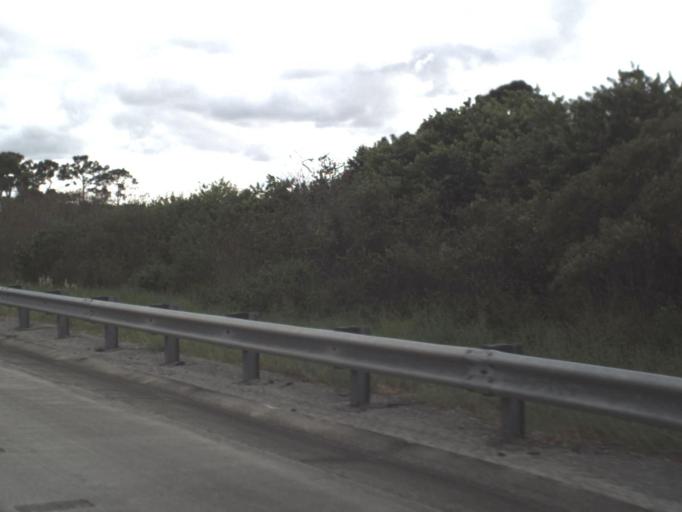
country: US
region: Florida
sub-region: Martin County
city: Port Salerno
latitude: 27.0682
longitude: -80.2452
